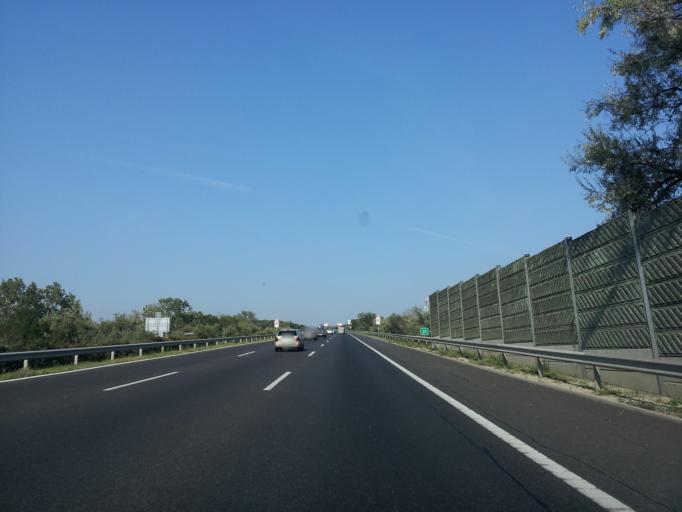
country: HU
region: Pest
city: Tarnok
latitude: 47.3919
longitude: 18.8538
